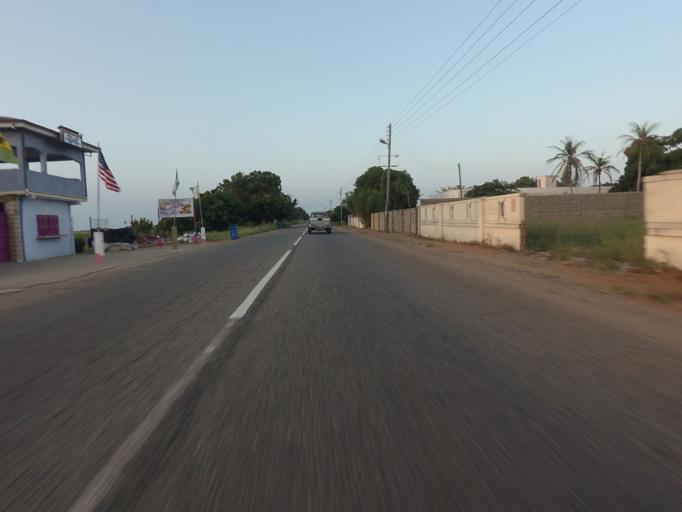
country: GH
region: Volta
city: Anloga
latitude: 5.8194
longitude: 0.9431
